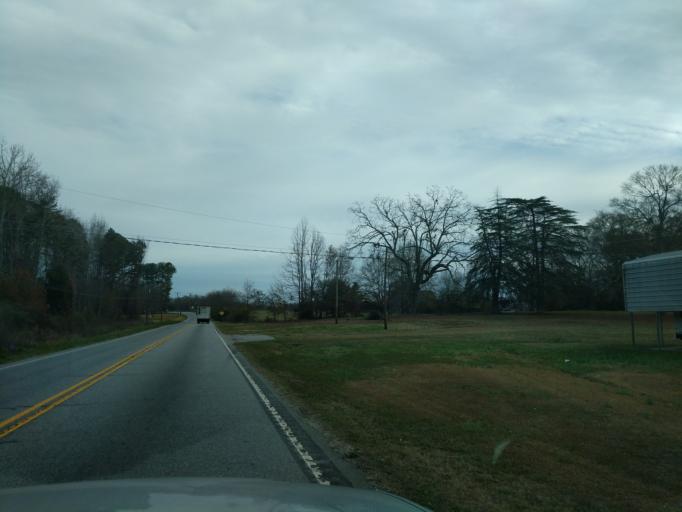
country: US
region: South Carolina
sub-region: Anderson County
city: Piedmont
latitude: 34.6718
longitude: -82.5292
